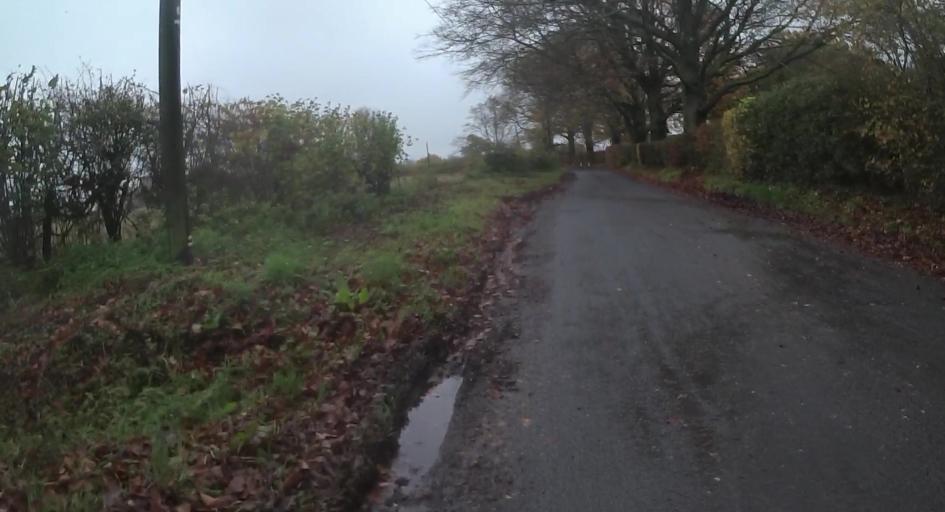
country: GB
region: England
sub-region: Hampshire
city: Four Marks
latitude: 51.1471
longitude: -1.1110
